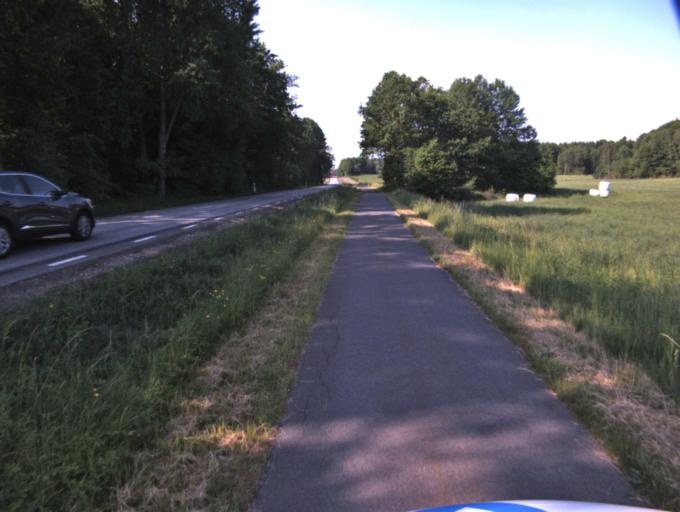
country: SE
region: Skane
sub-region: Kristianstads Kommun
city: Tollarp
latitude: 56.1612
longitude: 14.2739
